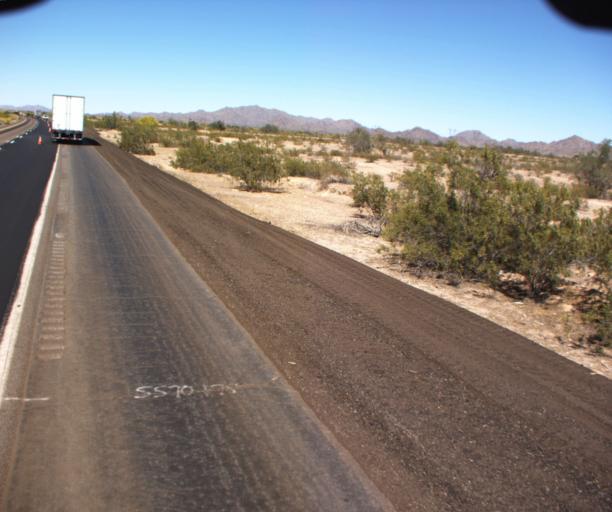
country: US
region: Arizona
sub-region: Maricopa County
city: Gila Bend
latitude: 33.0499
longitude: -112.6435
